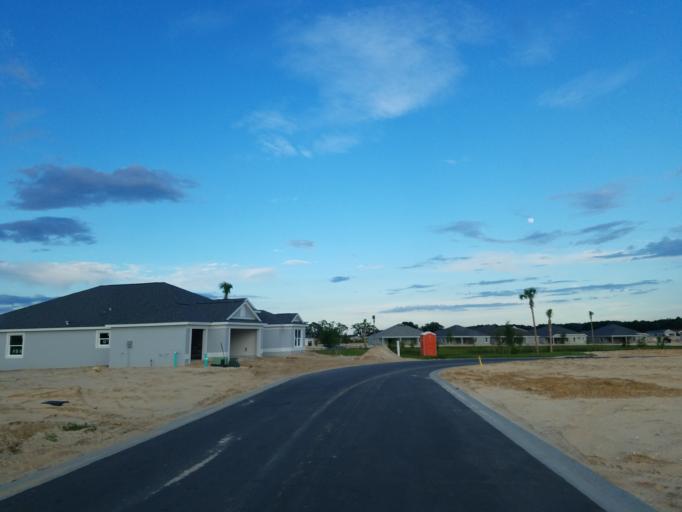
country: US
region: Florida
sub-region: Sumter County
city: Wildwood
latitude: 28.7890
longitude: -82.0166
